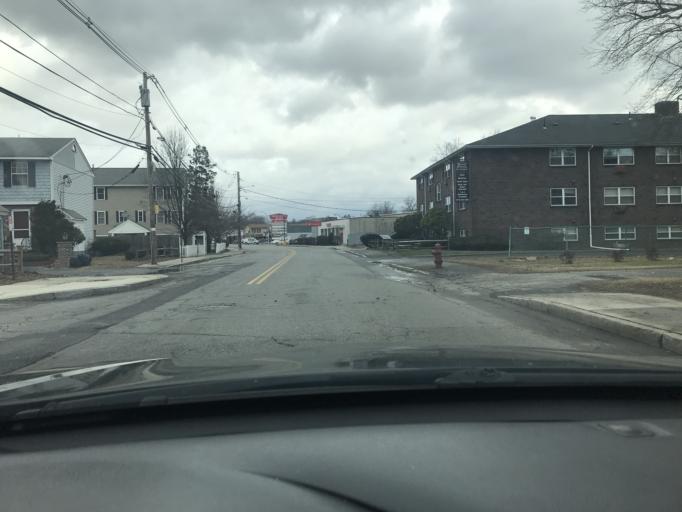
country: US
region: Massachusetts
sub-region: Middlesex County
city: Chelmsford
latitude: 42.6349
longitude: -71.3580
